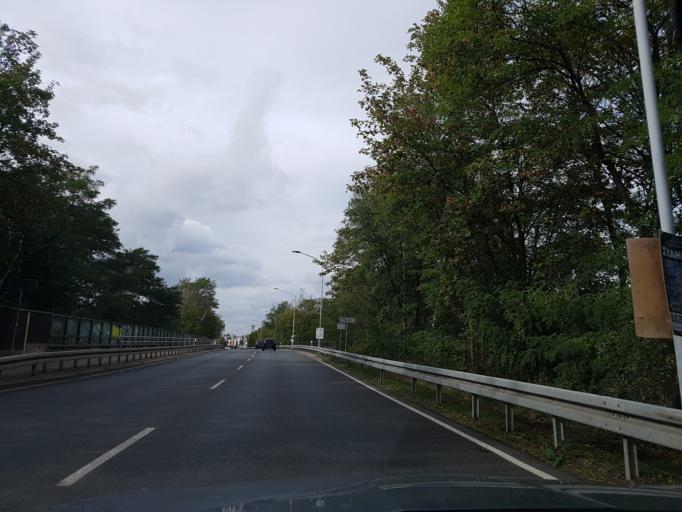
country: DE
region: Saxony
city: Riesa
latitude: 51.2935
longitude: 13.2911
